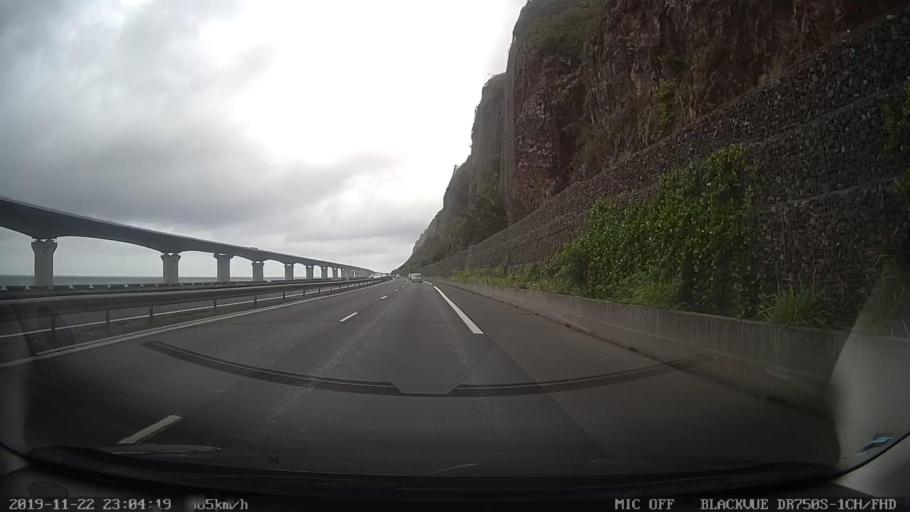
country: RE
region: Reunion
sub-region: Reunion
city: Saint-Denis
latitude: -20.8818
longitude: 55.3967
